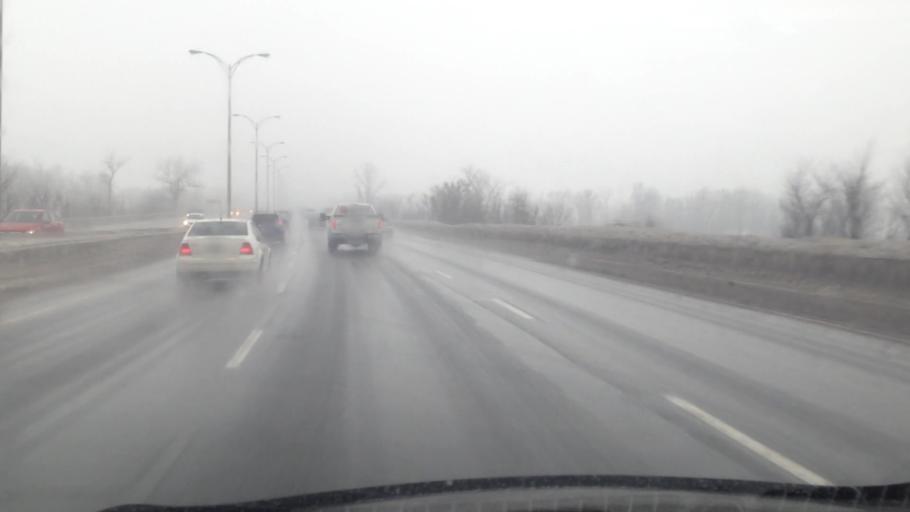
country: CA
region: Quebec
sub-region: Laurentides
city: Boisbriand
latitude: 45.6066
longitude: -73.8075
